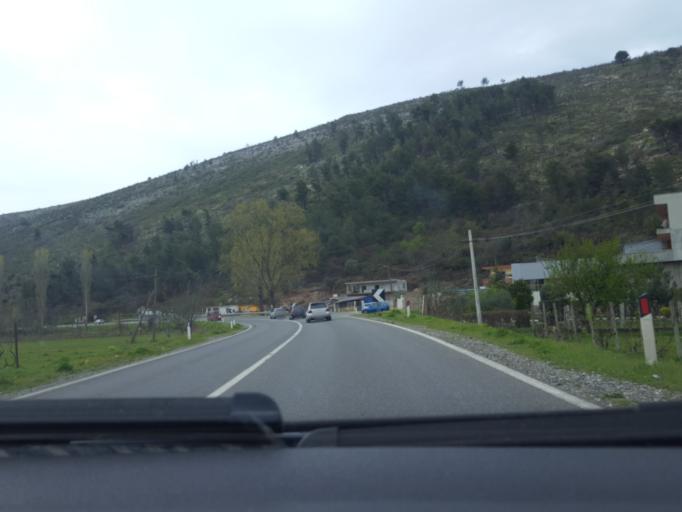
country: AL
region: Lezhe
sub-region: Rrethi i Lezhes
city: Balldreni i Ri
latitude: 41.8033
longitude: 19.6307
